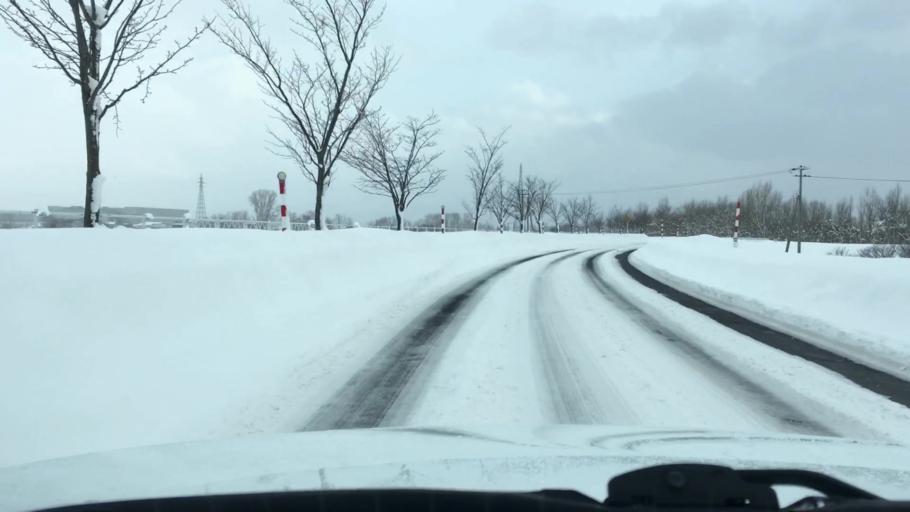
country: JP
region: Aomori
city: Hirosaki
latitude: 40.6512
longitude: 140.4732
